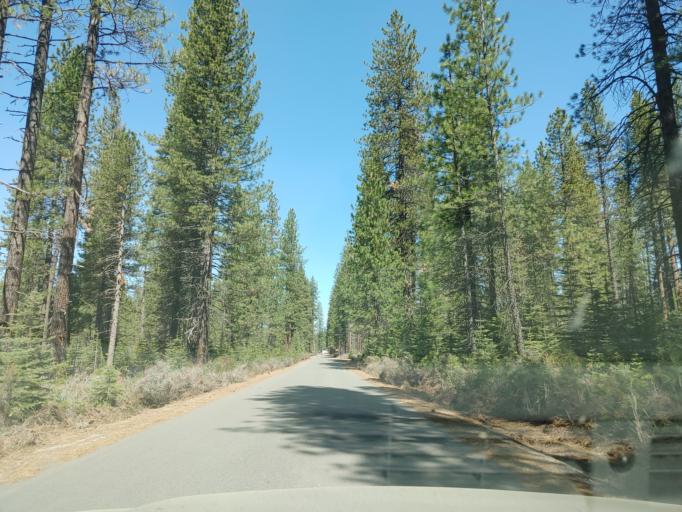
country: US
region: California
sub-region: Siskiyou County
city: McCloud
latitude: 41.2611
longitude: -121.9426
